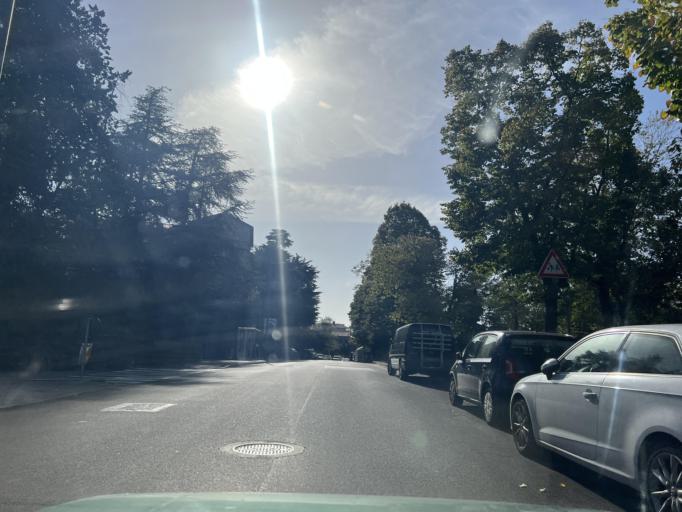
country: IT
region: Friuli Venezia Giulia
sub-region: Provincia di Trieste
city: Domio
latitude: 45.6187
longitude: 13.8257
